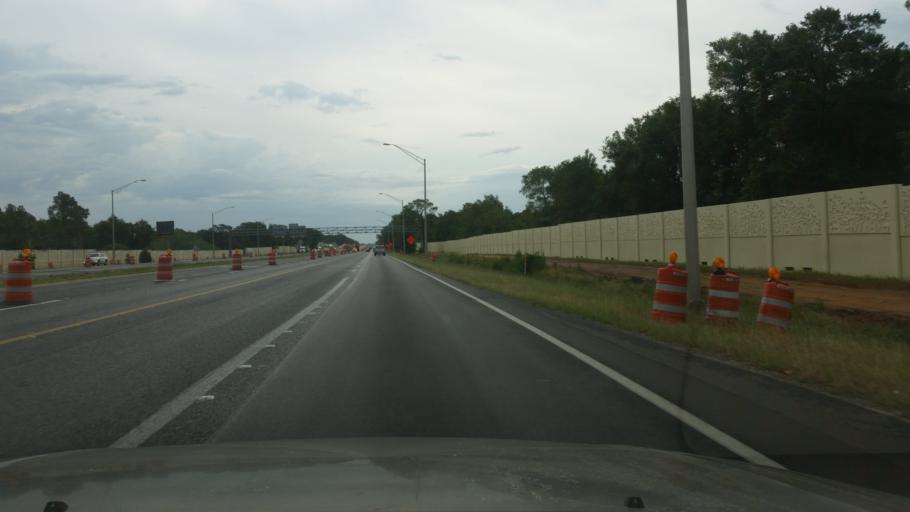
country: US
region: Florida
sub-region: Escambia County
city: Ferry Pass
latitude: 30.5028
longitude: -87.2109
